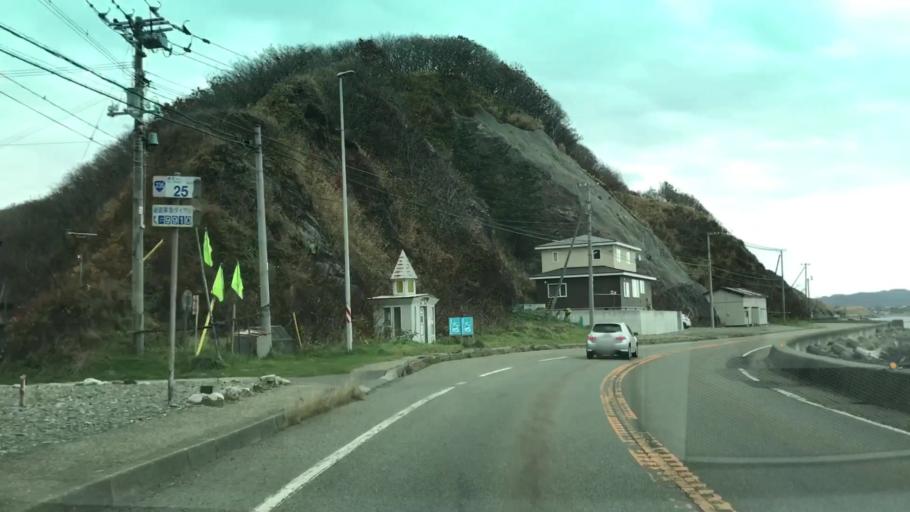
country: JP
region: Hokkaido
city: Shizunai-furukawacho
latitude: 42.0565
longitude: 143.0791
